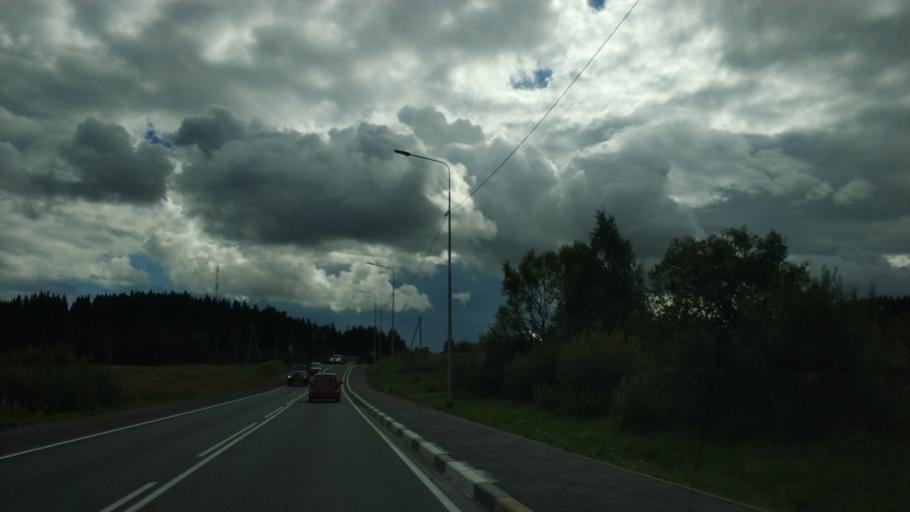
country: RU
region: Republic of Karelia
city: Khelyulya
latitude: 61.7604
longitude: 30.6570
